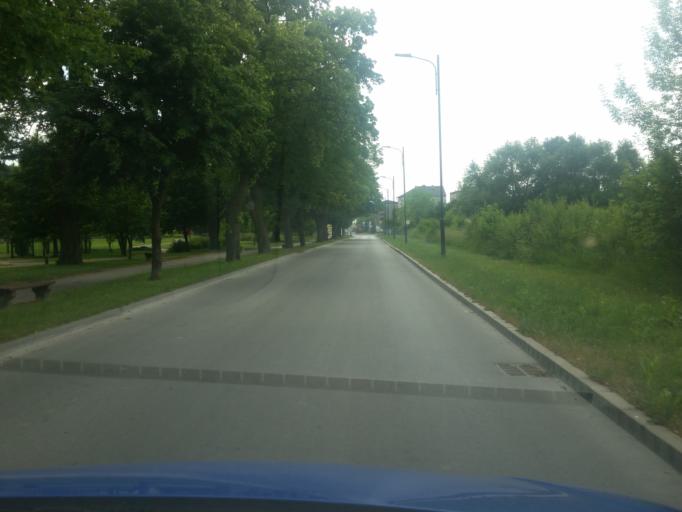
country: PL
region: Swietokrzyskie
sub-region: Powiat buski
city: Busko-Zdroj
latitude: 50.4592
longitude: 20.7130
